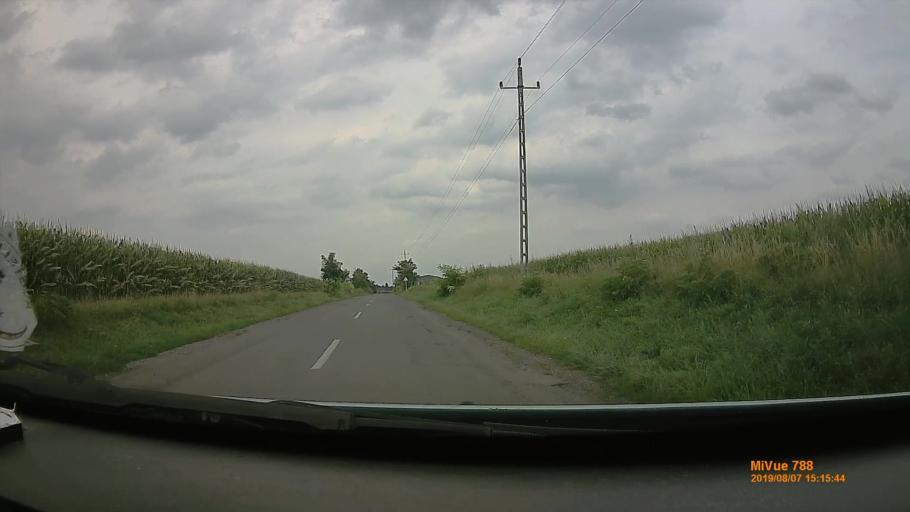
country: HU
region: Borsod-Abauj-Zemplen
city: Encs
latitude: 48.3413
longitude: 21.1318
